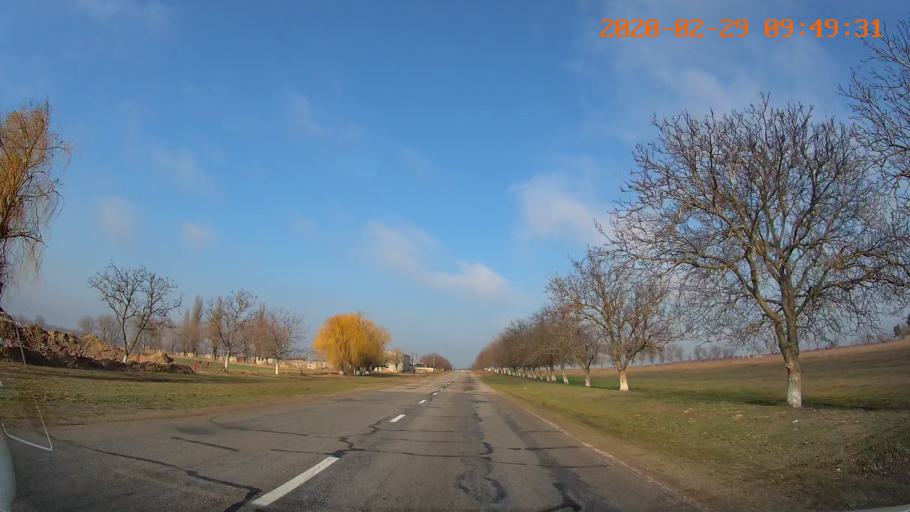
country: MD
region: Telenesti
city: Crasnoe
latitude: 46.6976
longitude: 29.7710
